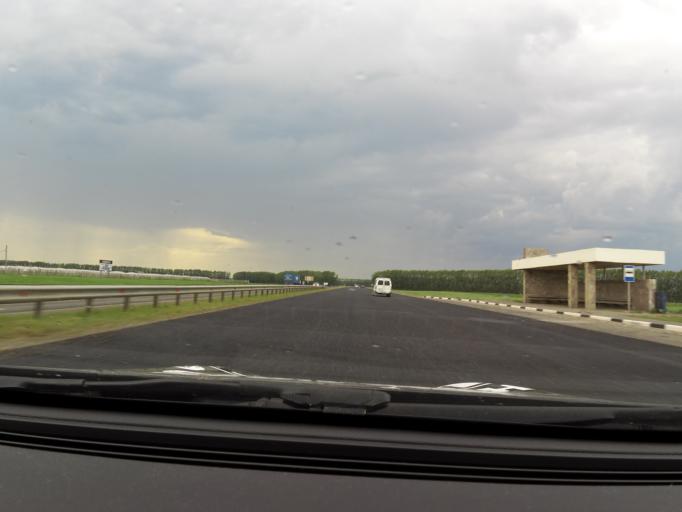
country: RU
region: Bashkortostan
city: Asanovo
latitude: 54.9813
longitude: 55.5479
